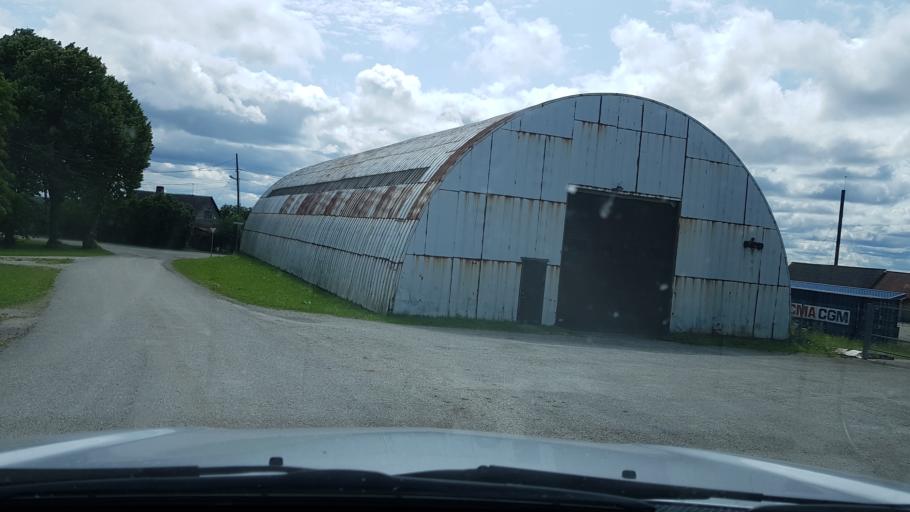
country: EE
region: Ida-Virumaa
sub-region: Sillamaee linn
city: Sillamae
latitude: 59.3740
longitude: 27.8679
